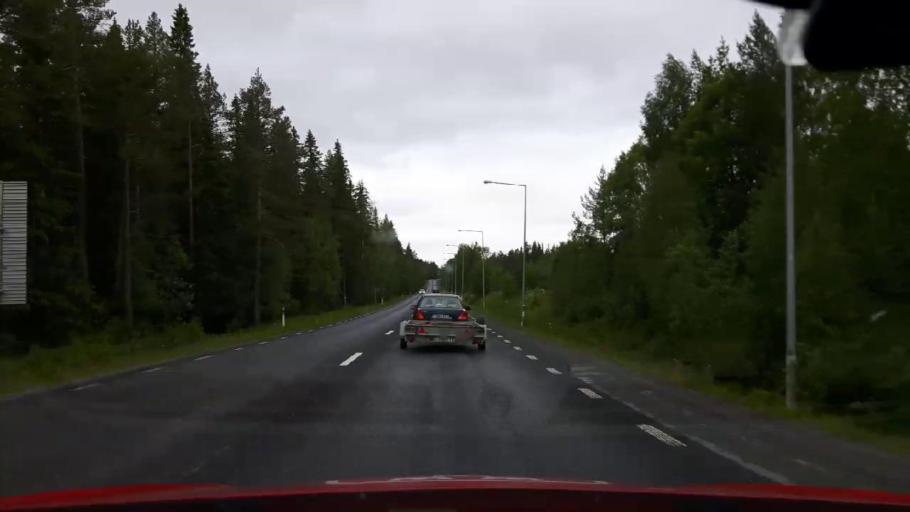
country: SE
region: Jaemtland
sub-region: OEstersunds Kommun
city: Ostersund
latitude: 63.1998
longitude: 14.6724
